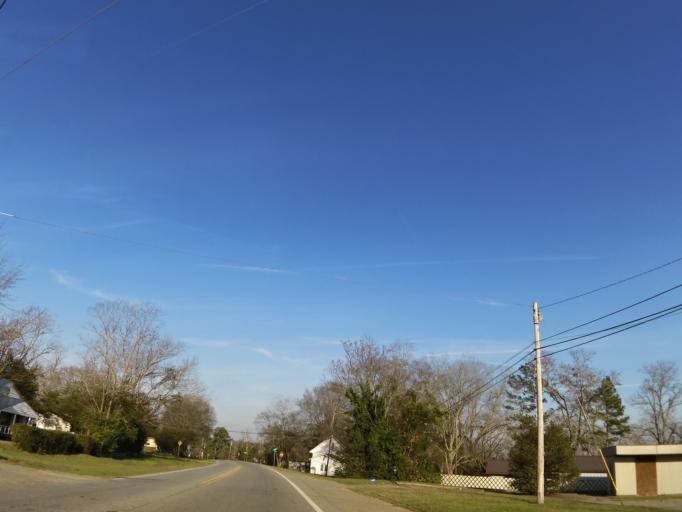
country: US
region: Georgia
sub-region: Stewart County
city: Richland
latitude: 32.0886
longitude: -84.6536
